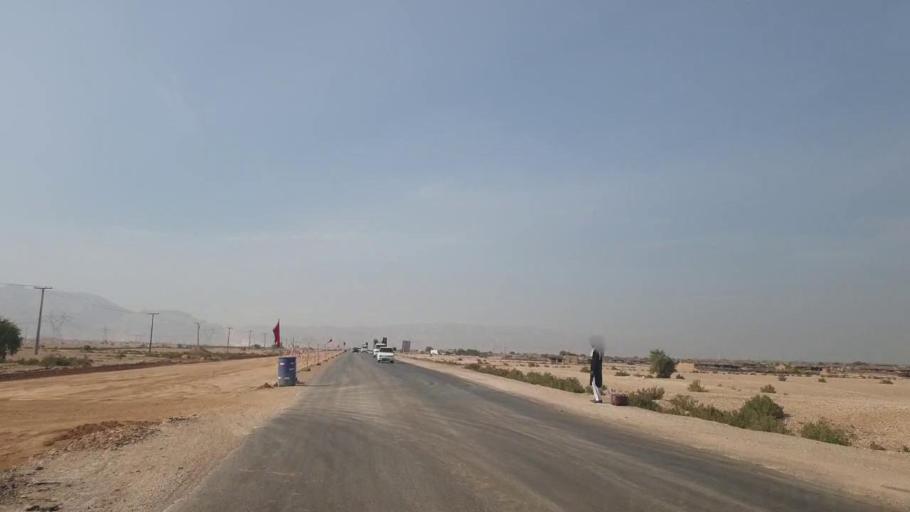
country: PK
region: Sindh
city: Sehwan
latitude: 26.1981
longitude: 67.9420
